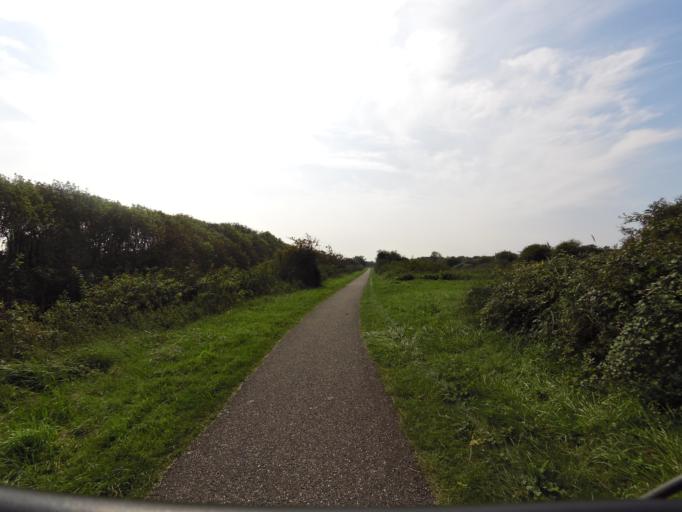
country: NL
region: Zeeland
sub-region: Gemeente Noord-Beveland
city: Kamperland
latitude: 51.5943
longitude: 3.6687
